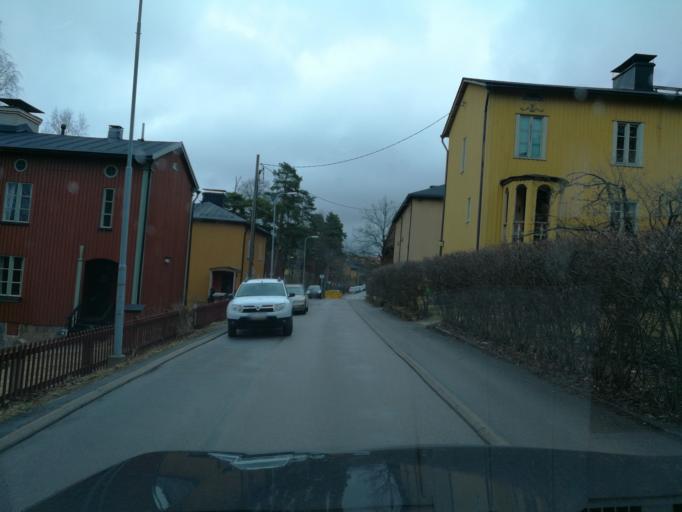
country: FI
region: Uusimaa
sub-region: Helsinki
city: Helsinki
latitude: 60.2146
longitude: 24.9517
